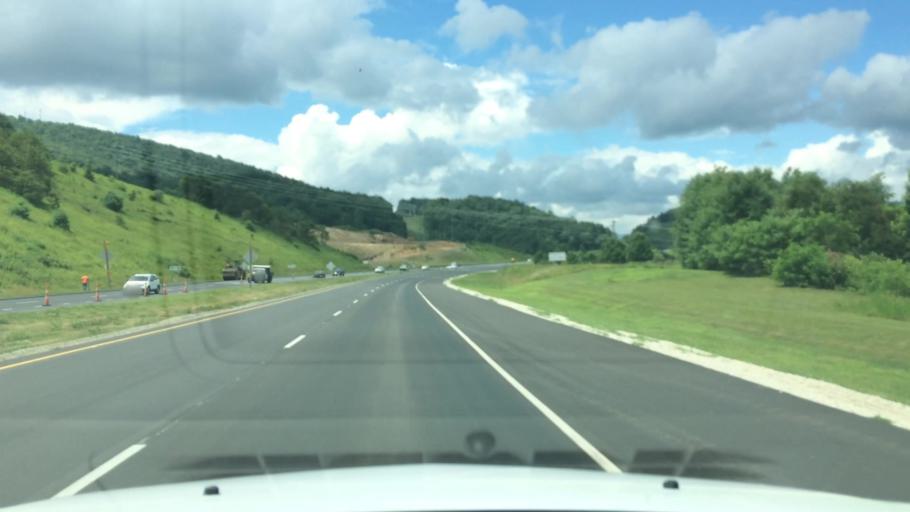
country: US
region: North Carolina
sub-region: Watauga County
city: Boone
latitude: 36.2261
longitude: -81.6082
